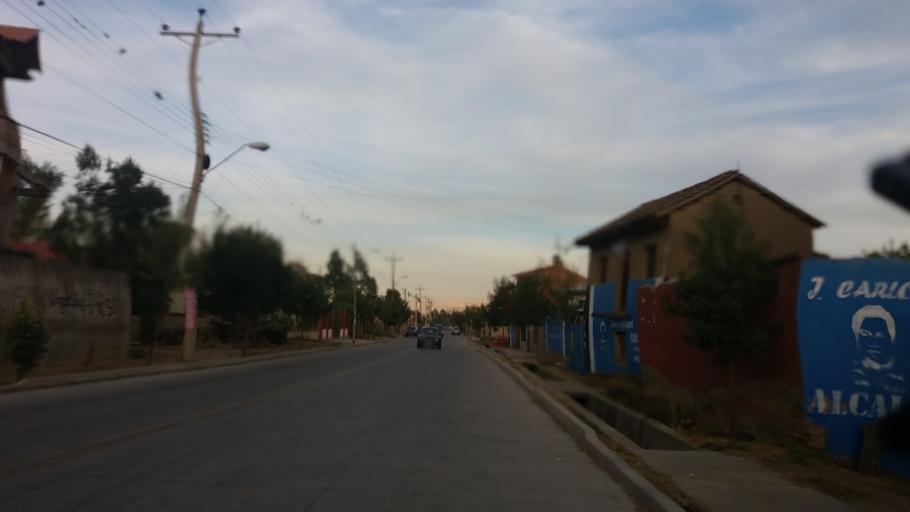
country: BO
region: Cochabamba
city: Cochabamba
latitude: -17.3654
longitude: -66.2177
